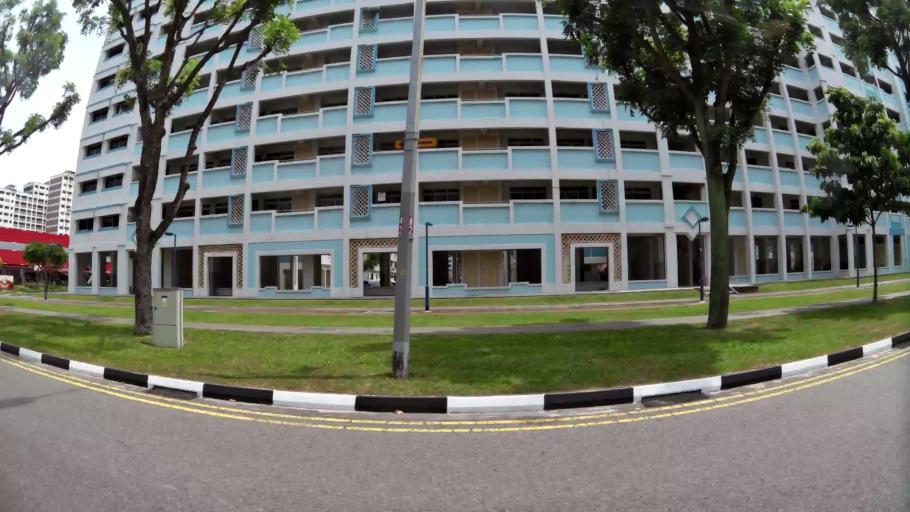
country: MY
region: Johor
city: Johor Bahru
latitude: 1.3479
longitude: 103.6971
